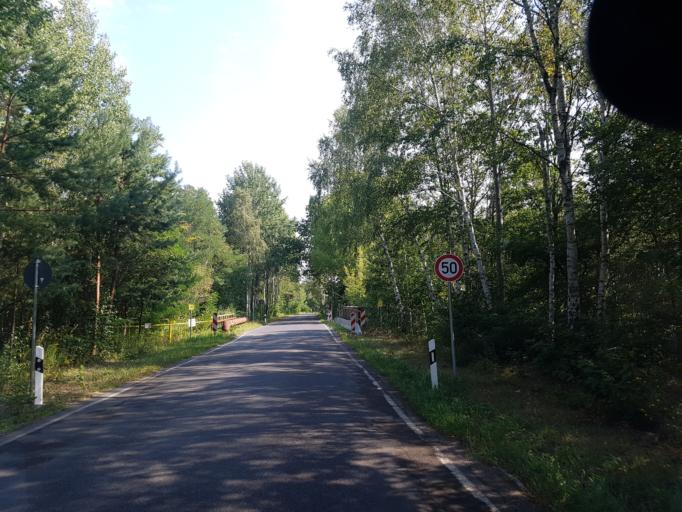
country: DE
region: Brandenburg
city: Lauchhammer
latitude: 51.5112
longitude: 13.7359
